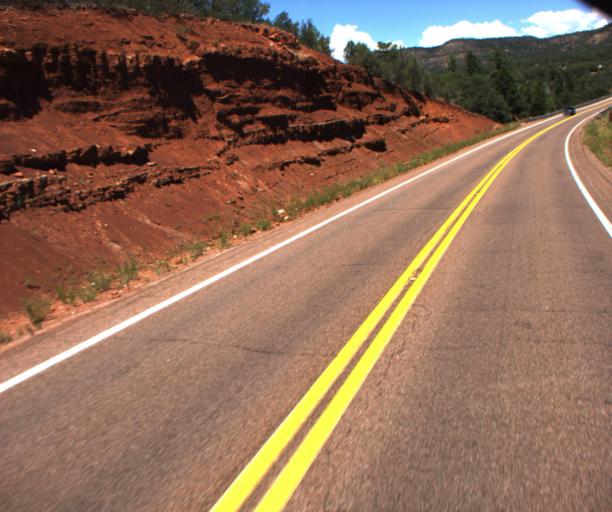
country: US
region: Arizona
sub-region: Navajo County
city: Cibecue
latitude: 33.9525
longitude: -110.3319
